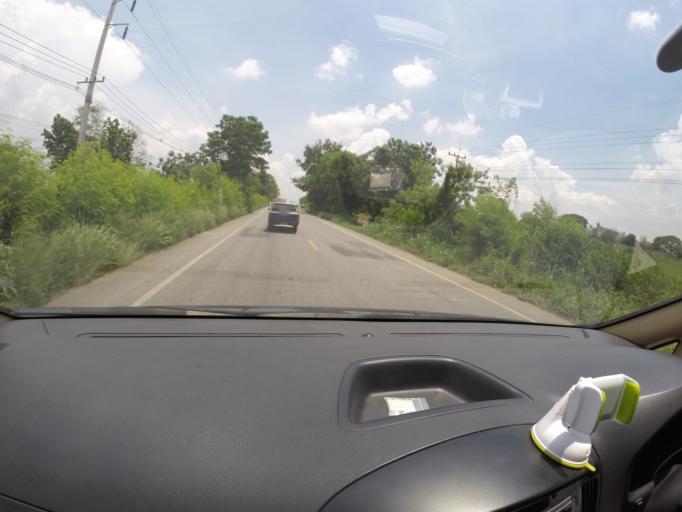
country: TH
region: Nakhon Ratchasima
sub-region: Amphoe Thepharak
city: Thepharak
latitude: 15.1256
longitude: 101.5408
